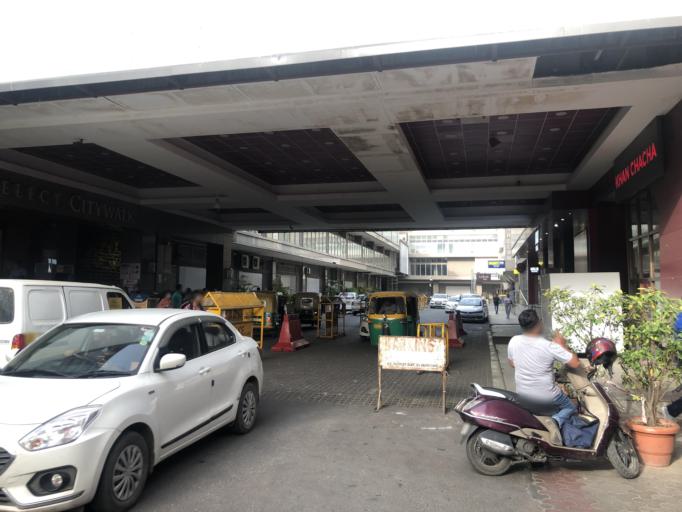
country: IN
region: NCT
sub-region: New Delhi
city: New Delhi
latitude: 28.5282
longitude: 77.2192
